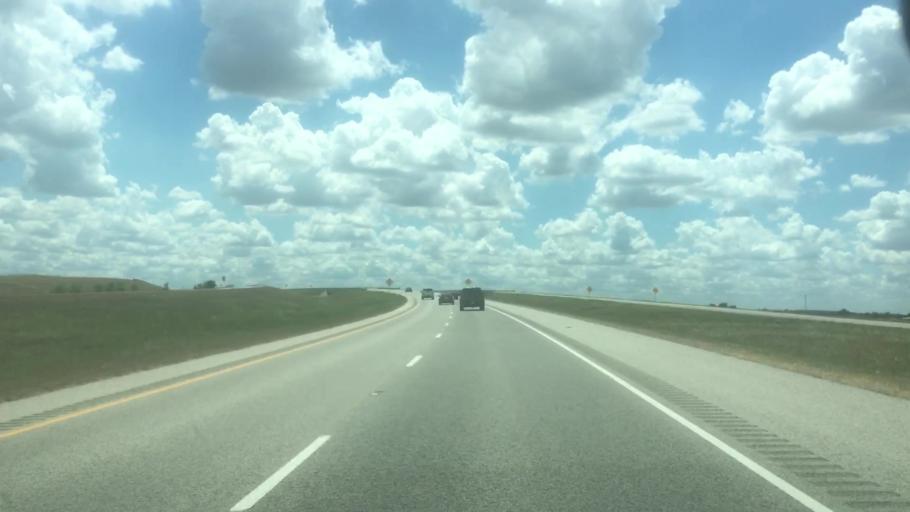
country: US
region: Texas
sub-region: Caldwell County
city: Lockhart
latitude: 29.8924
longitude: -97.7125
